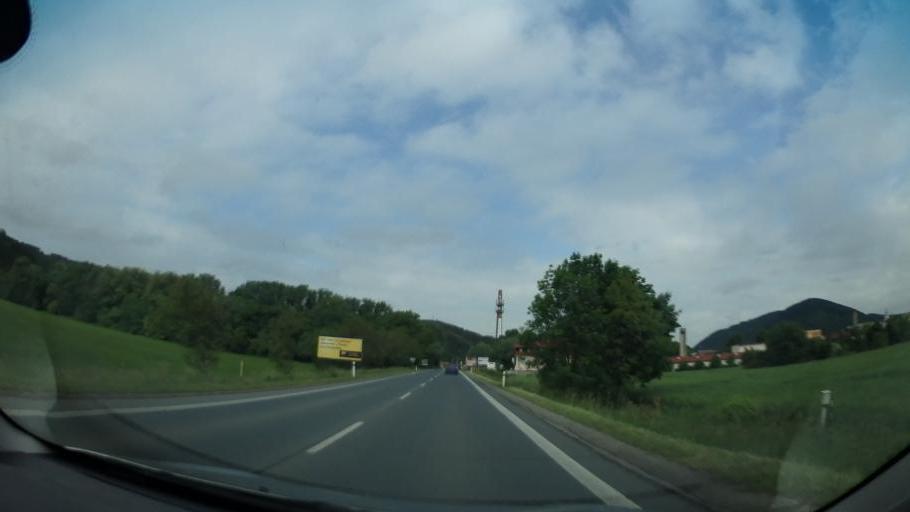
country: CZ
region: South Moravian
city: Tisnov
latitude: 49.3388
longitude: 16.4257
